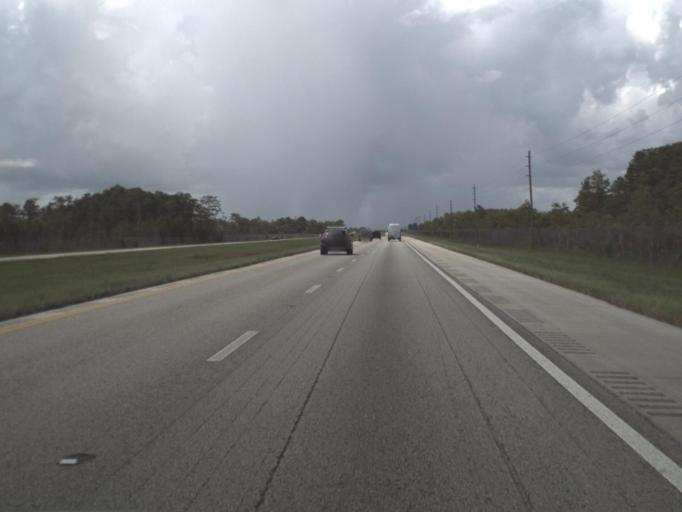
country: US
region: Florida
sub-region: Collier County
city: Immokalee
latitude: 26.1553
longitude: -81.3017
